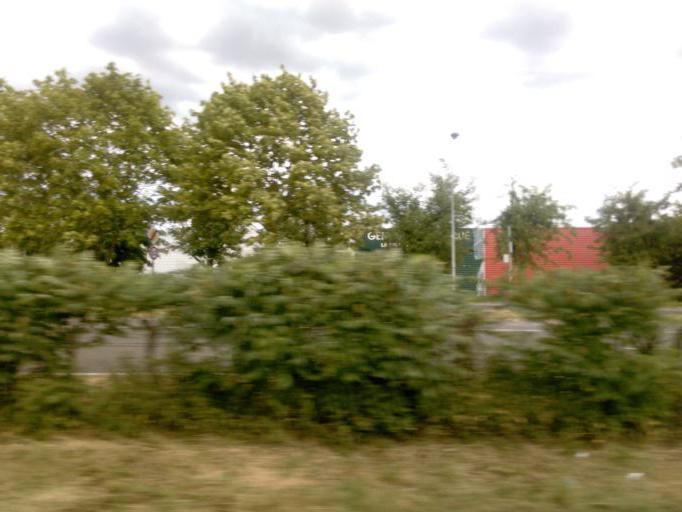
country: FR
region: Ile-de-France
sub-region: Departement du Val-d'Oise
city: Osny
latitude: 49.0760
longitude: 2.0757
